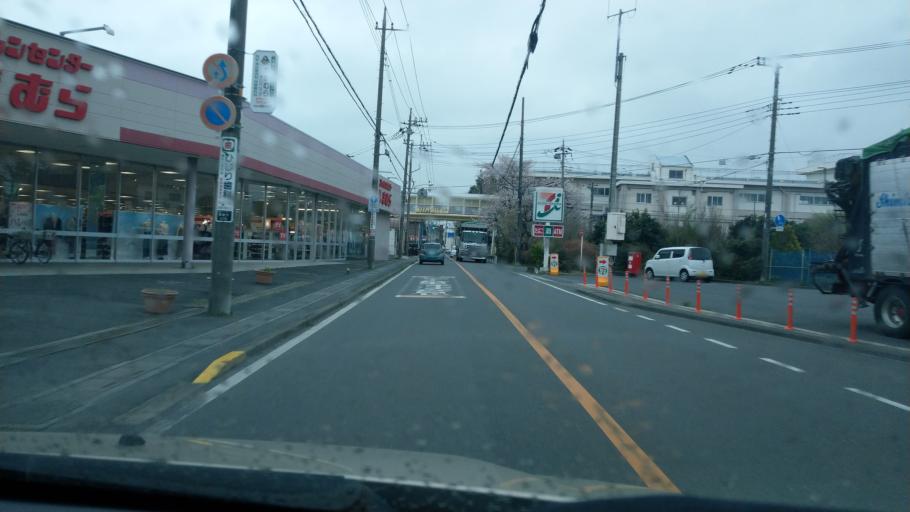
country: JP
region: Saitama
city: Iwatsuki
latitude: 35.9303
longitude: 139.6753
